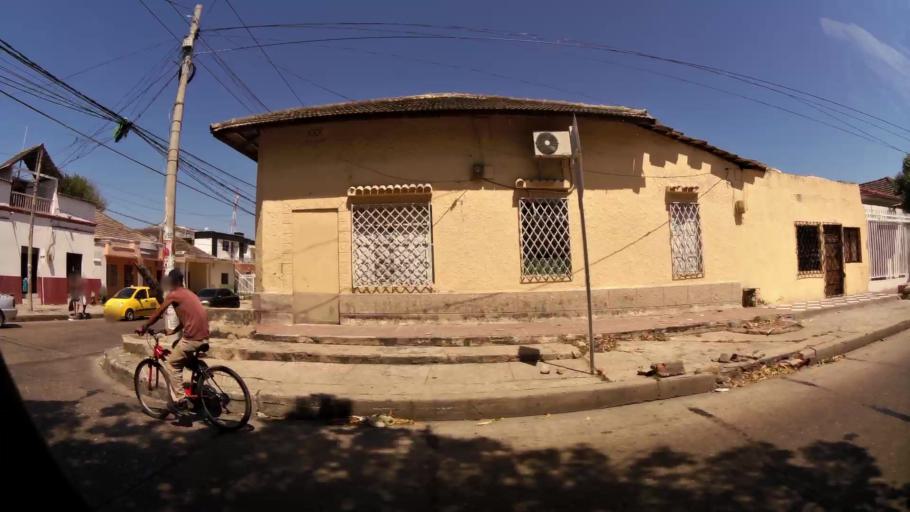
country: CO
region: Atlantico
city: Barranquilla
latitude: 10.9898
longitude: -74.7972
